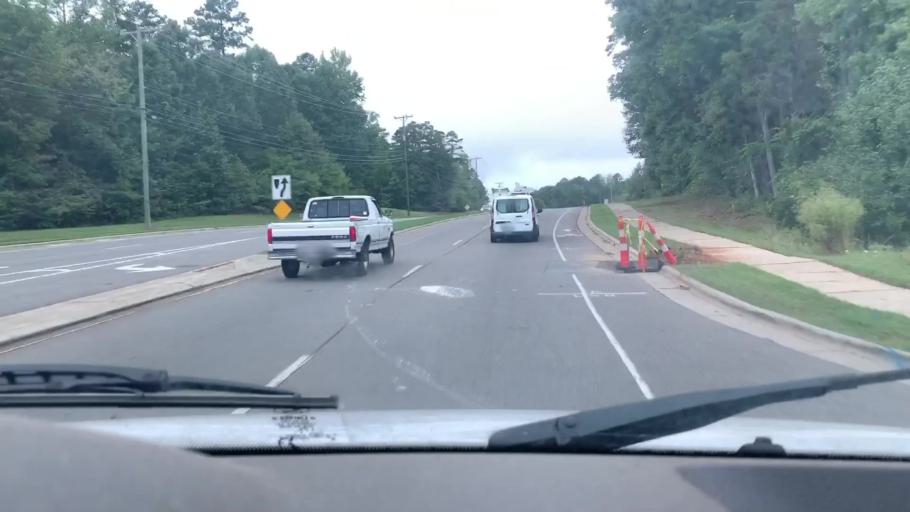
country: US
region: North Carolina
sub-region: Iredell County
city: Mooresville
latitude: 35.5806
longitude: -80.8618
